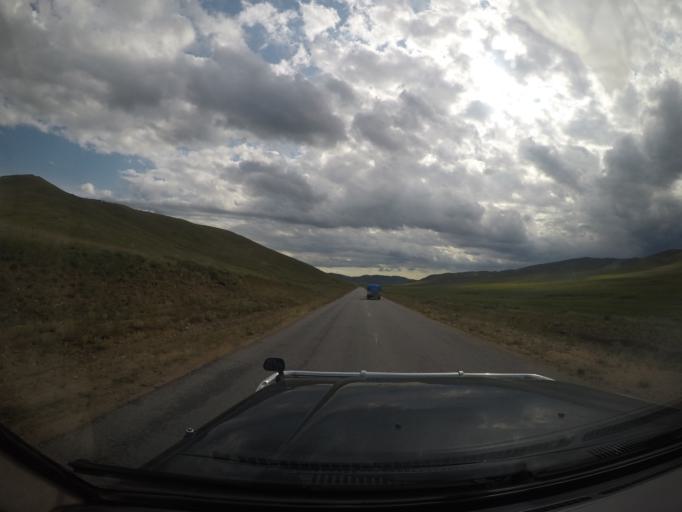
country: MN
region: Hentiy
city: Modot
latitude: 47.7295
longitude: 108.5913
